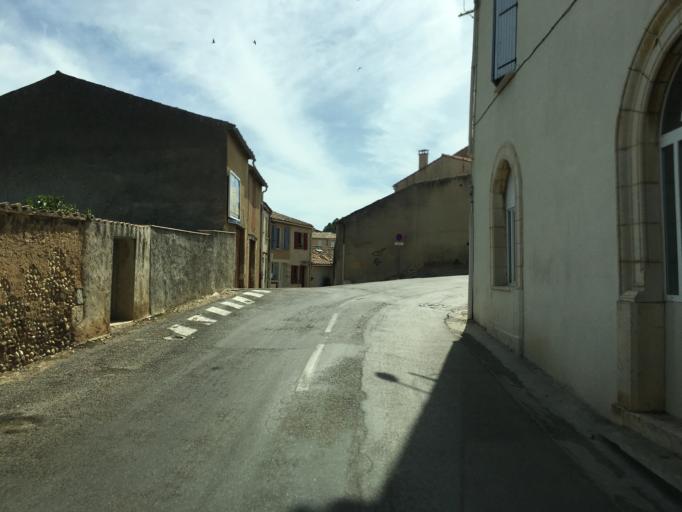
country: FR
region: Provence-Alpes-Cote d'Azur
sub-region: Departement des Alpes-de-Haute-Provence
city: Valensole
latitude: 43.8378
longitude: 5.9864
